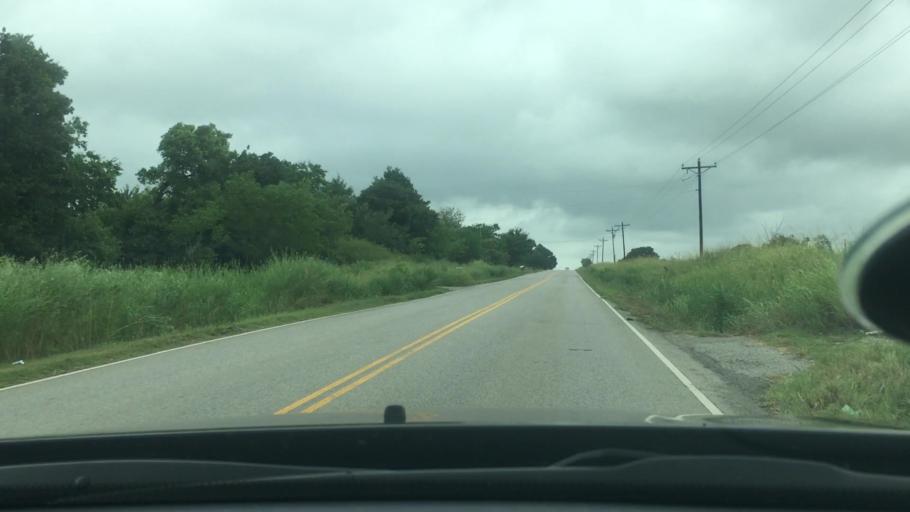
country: US
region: Oklahoma
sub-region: Bryan County
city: Calera
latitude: 33.9468
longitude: -96.5005
